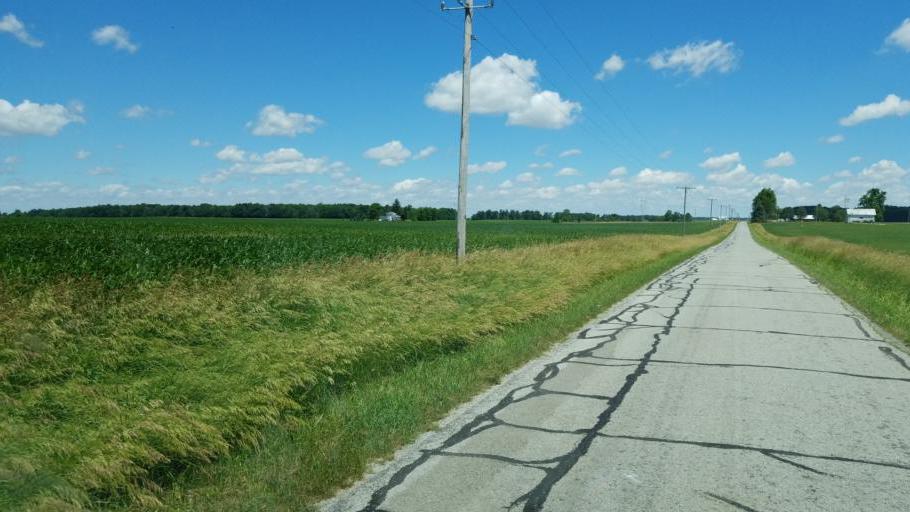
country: US
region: Ohio
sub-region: Crawford County
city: Bucyrus
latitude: 40.7347
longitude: -82.9366
